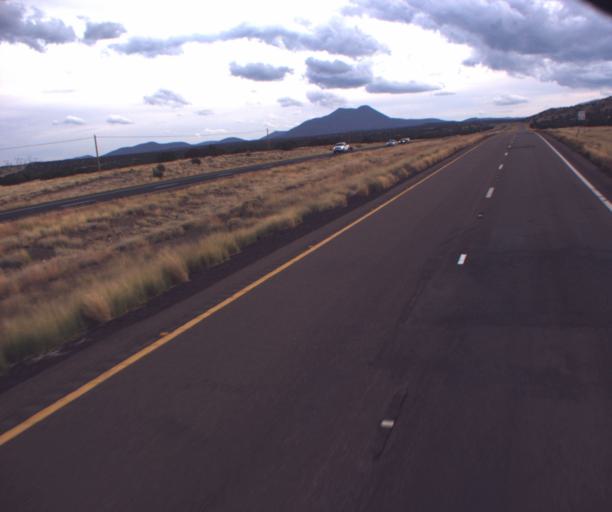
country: US
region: Arizona
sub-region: Coconino County
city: Flagstaff
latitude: 35.5344
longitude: -111.5407
